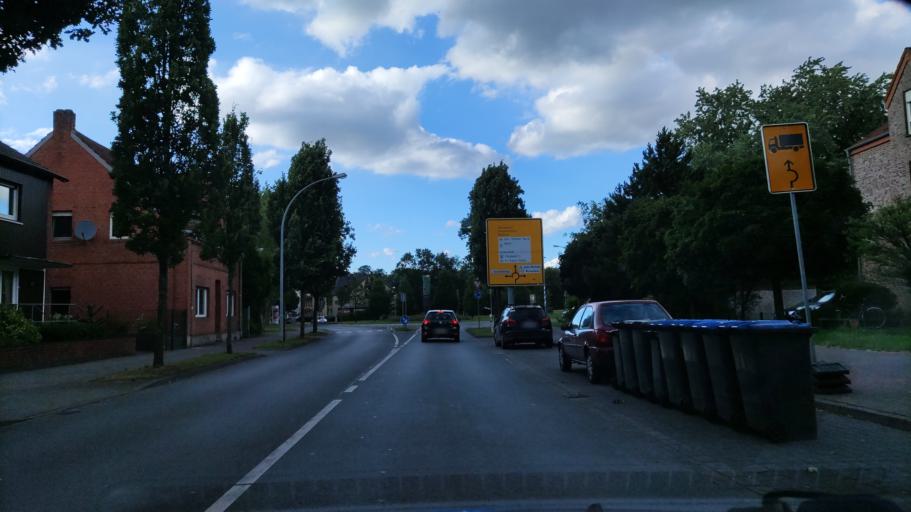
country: DE
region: North Rhine-Westphalia
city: Ahlen
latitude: 51.7531
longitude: 7.8980
